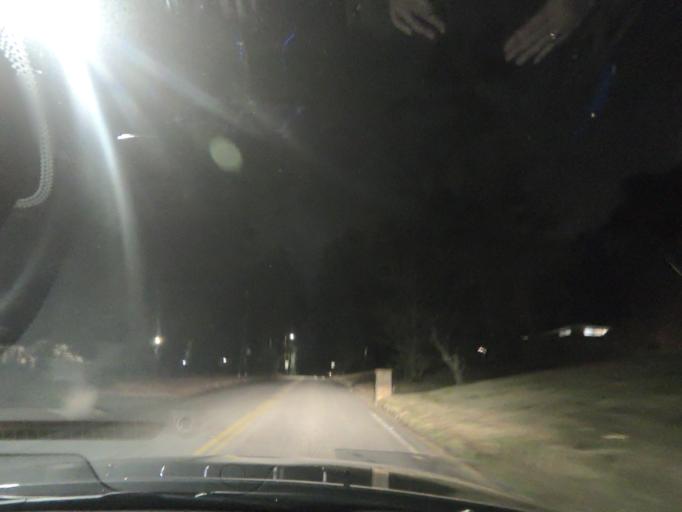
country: US
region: Georgia
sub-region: Fulton County
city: East Point
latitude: 33.7106
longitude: -84.4866
